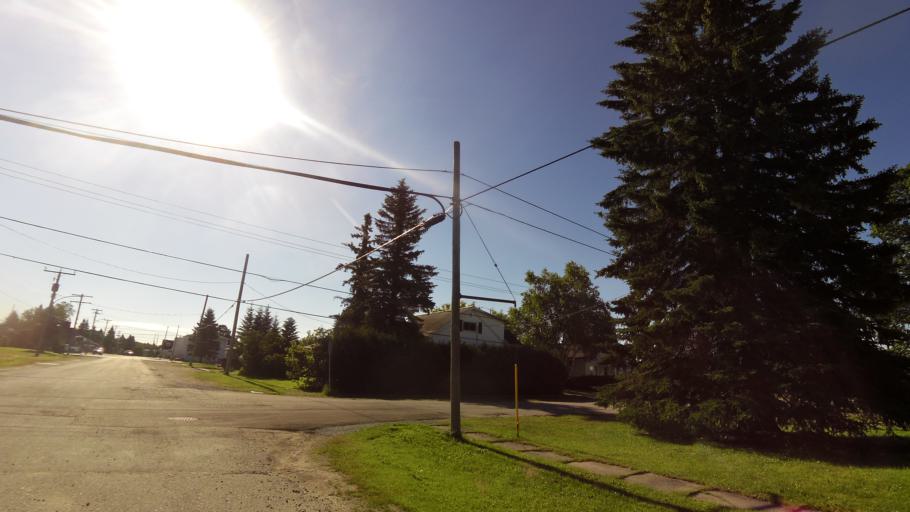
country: CA
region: Ontario
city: Iroquois Falls
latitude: 48.5361
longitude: -80.4686
